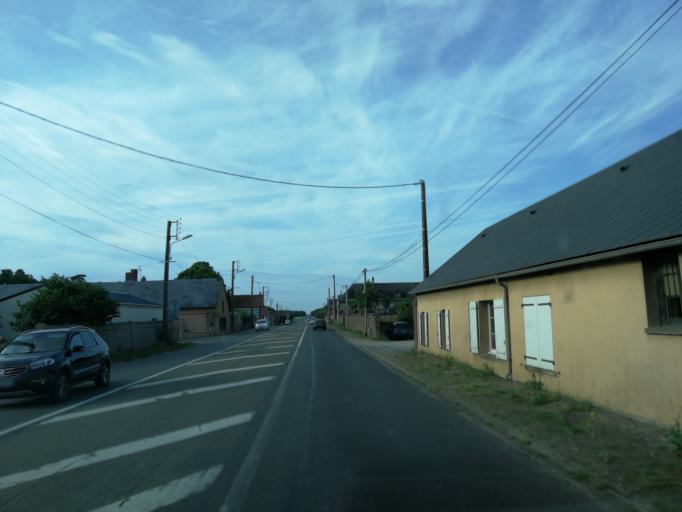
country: FR
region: Centre
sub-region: Departement d'Eure-et-Loir
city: Dammarie
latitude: 48.3249
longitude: 1.4316
